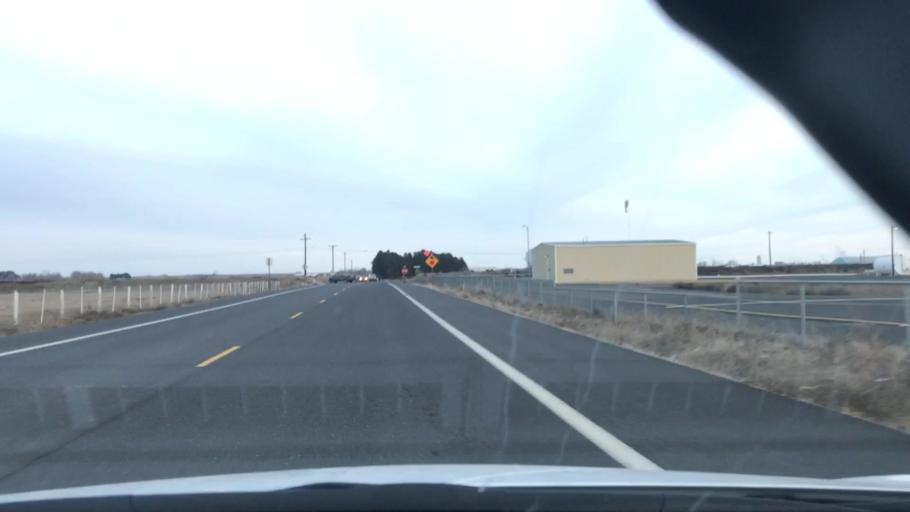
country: US
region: Washington
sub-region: Grant County
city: Moses Lake
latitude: 47.1456
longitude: -119.2381
